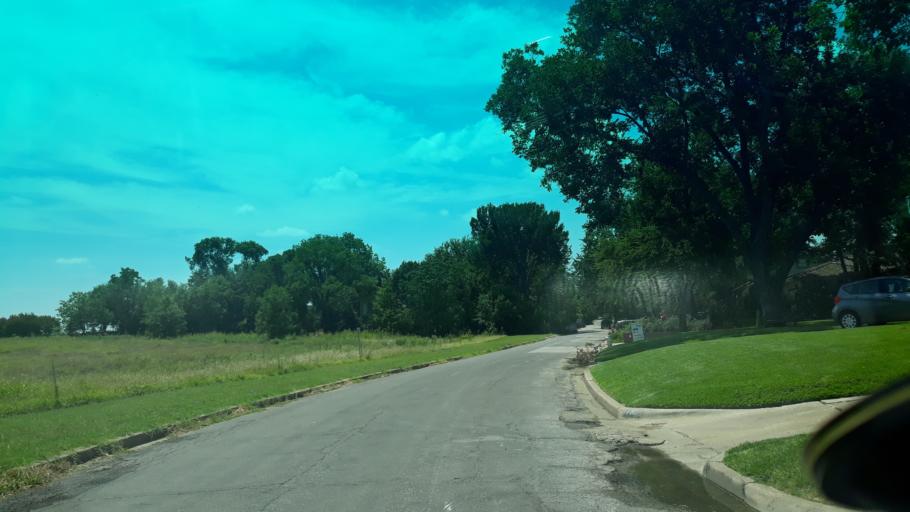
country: US
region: Texas
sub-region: Dallas County
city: Highland Park
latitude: 32.8230
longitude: -96.7321
